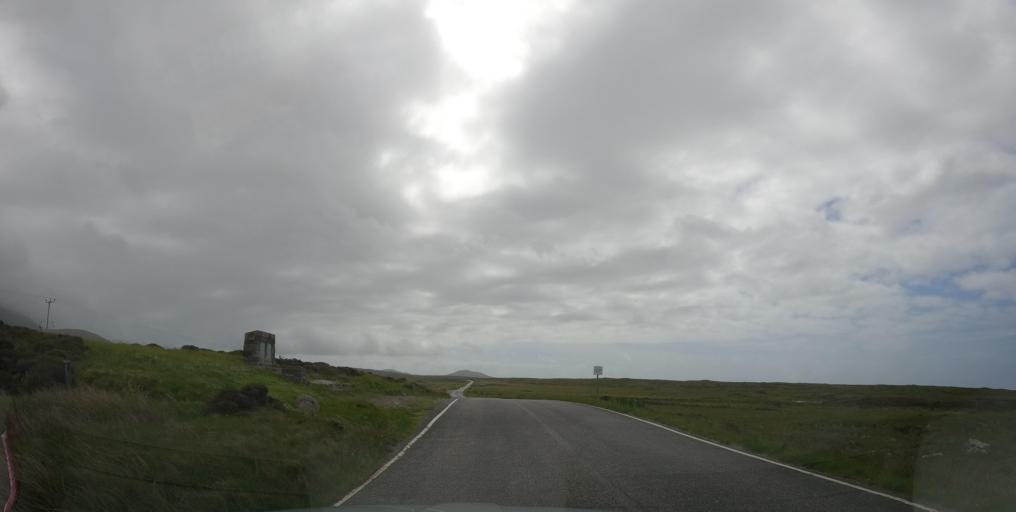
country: GB
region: Scotland
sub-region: Eilean Siar
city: Isle of South Uist
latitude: 57.2824
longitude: -7.3665
